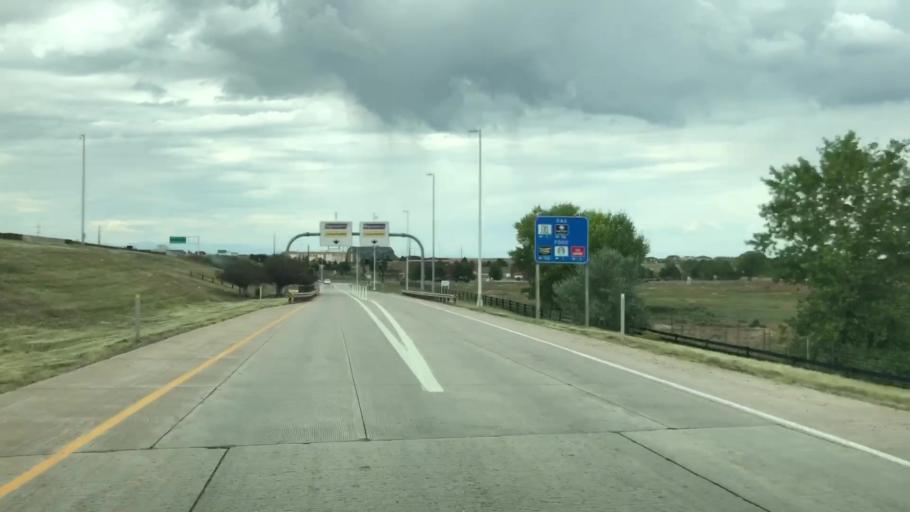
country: US
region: Colorado
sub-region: Douglas County
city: Stonegate
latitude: 39.5491
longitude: -104.7904
